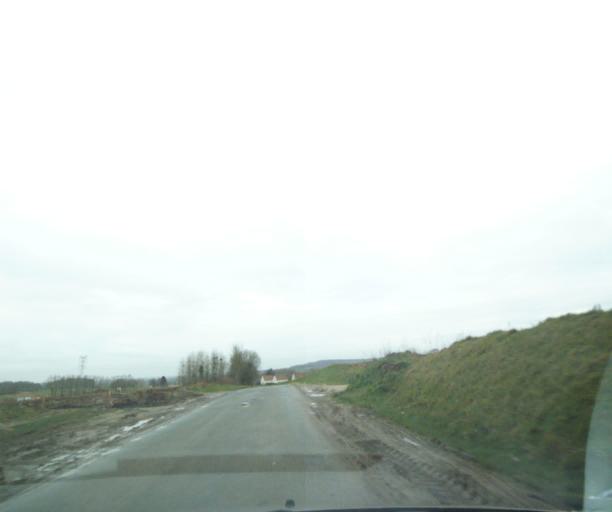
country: FR
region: Picardie
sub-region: Departement de l'Oise
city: Noyon
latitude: 49.5783
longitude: 2.9714
